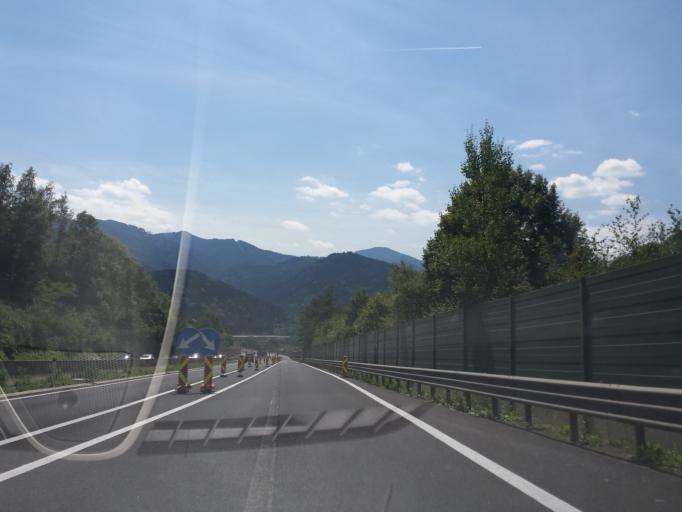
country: AT
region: Styria
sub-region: Politischer Bezirk Bruck-Muerzzuschlag
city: Bruck an der Mur
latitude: 47.4153
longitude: 15.2888
